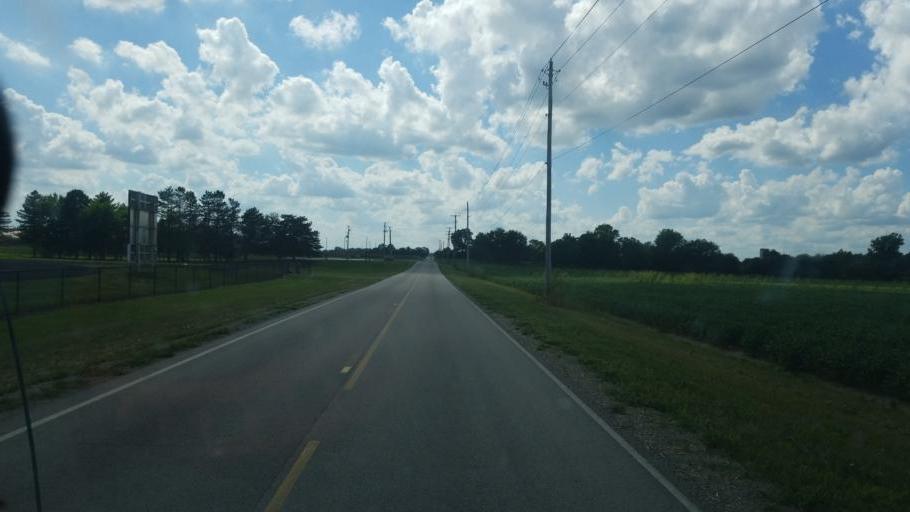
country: US
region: Ohio
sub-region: Union County
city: Richwood
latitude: 40.4392
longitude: -83.2990
